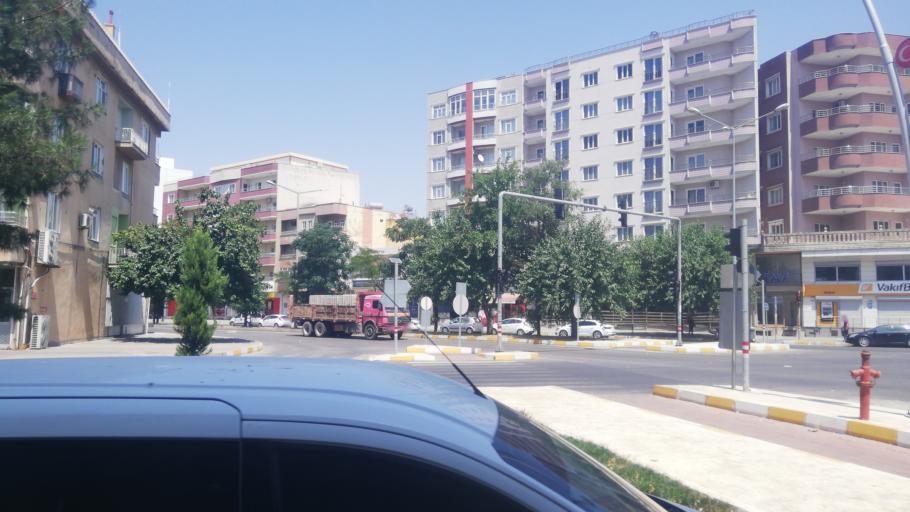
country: TR
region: Mardin
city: Midyat
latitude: 37.4226
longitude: 41.3462
